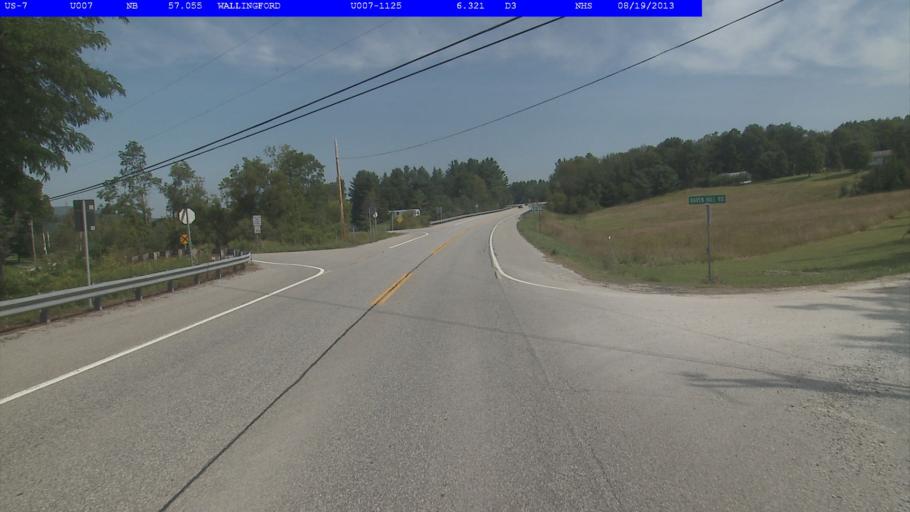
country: US
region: Vermont
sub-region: Rutland County
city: Rutland
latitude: 43.4834
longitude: -72.9735
